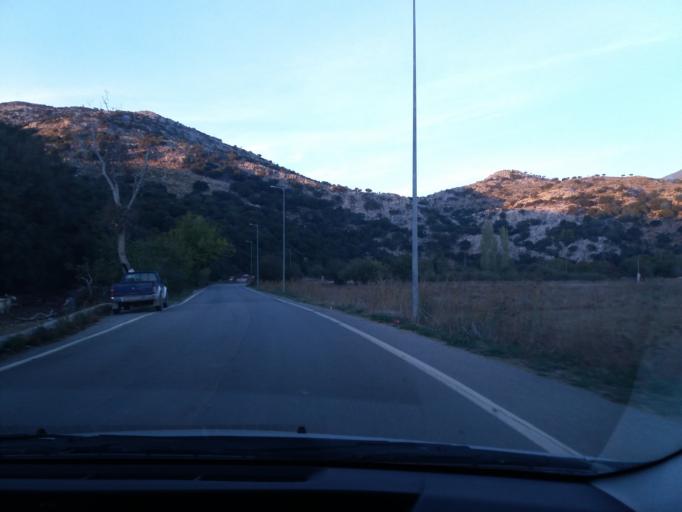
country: GR
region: Crete
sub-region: Nomos Irakleiou
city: Mokhos
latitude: 35.2022
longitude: 25.4742
